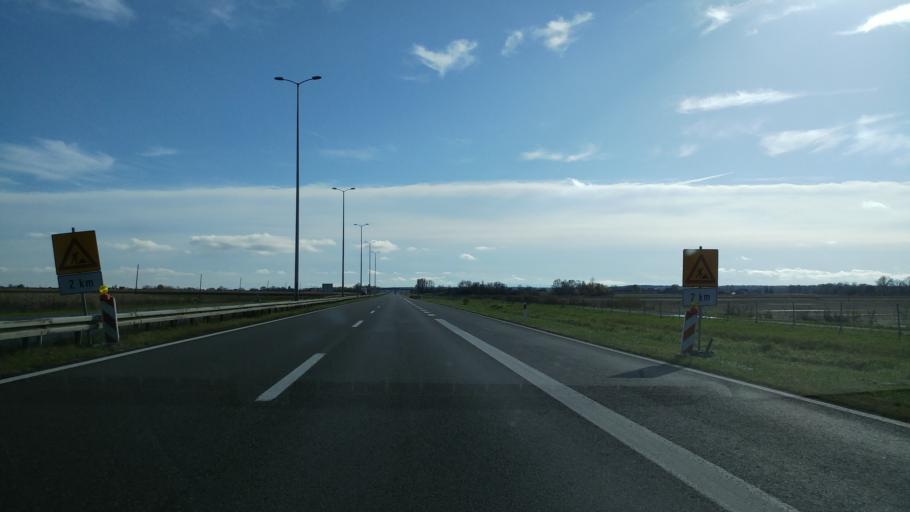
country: HR
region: Sisacko-Moslavacka
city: Lipovljani
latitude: 45.3987
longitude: 16.8622
